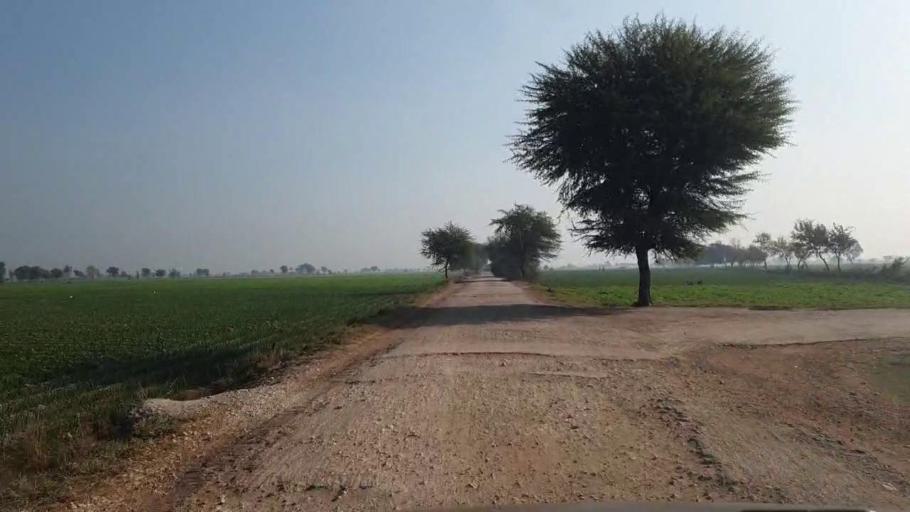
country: PK
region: Sindh
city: Shahdadpur
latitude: 26.0006
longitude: 68.6219
